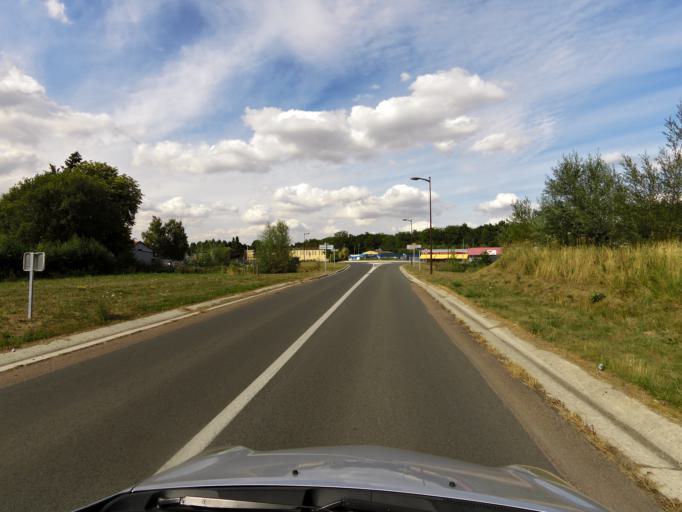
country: FR
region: Picardie
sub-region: Departement de l'Aisne
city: Bruyeres-et-Montberault
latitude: 49.5298
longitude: 3.6543
